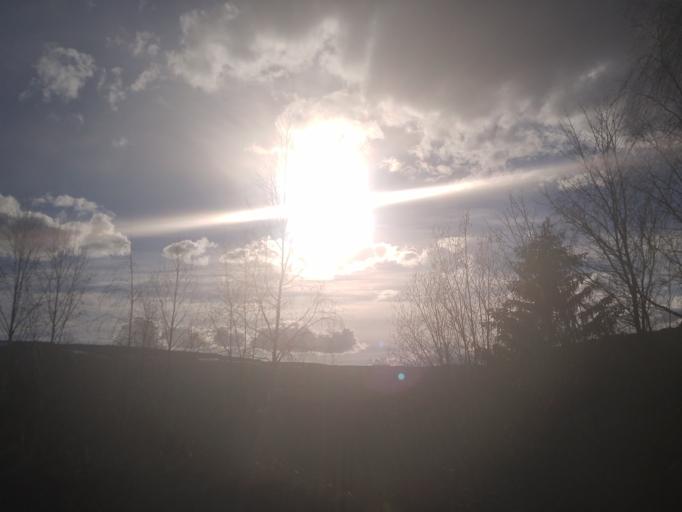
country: NO
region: Oppland
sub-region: Lillehammer
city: Lillehammer
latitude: 61.1605
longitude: 10.4044
